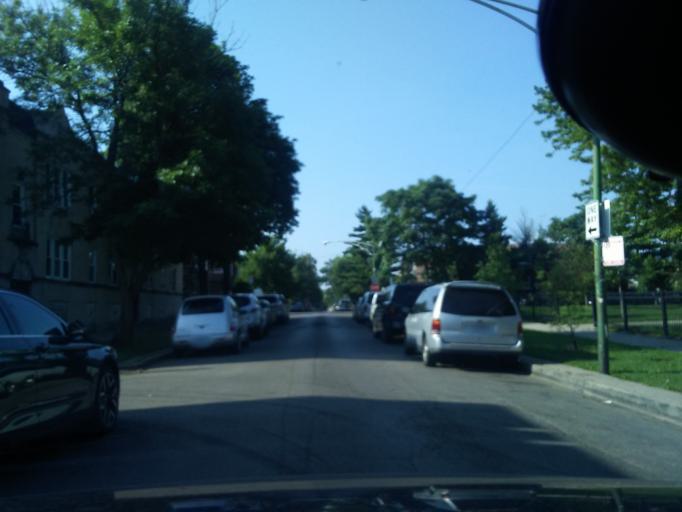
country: US
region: Illinois
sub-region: Cook County
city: Oak Park
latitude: 41.9229
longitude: -87.7511
